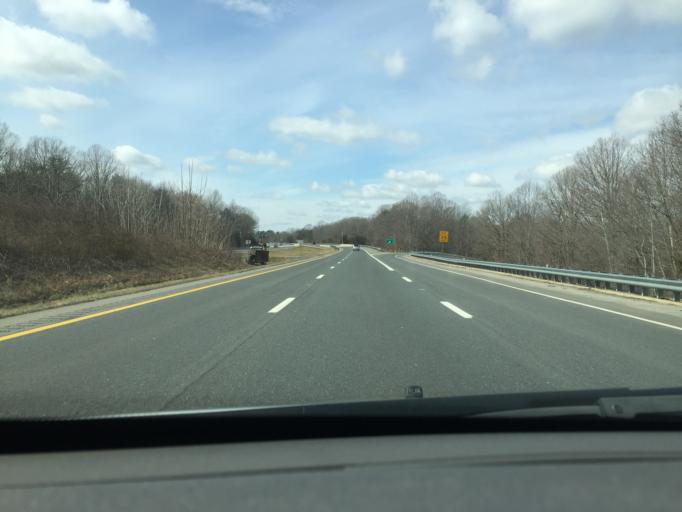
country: US
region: Virginia
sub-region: Campbell County
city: Timberlake
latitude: 37.3106
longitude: -79.2588
